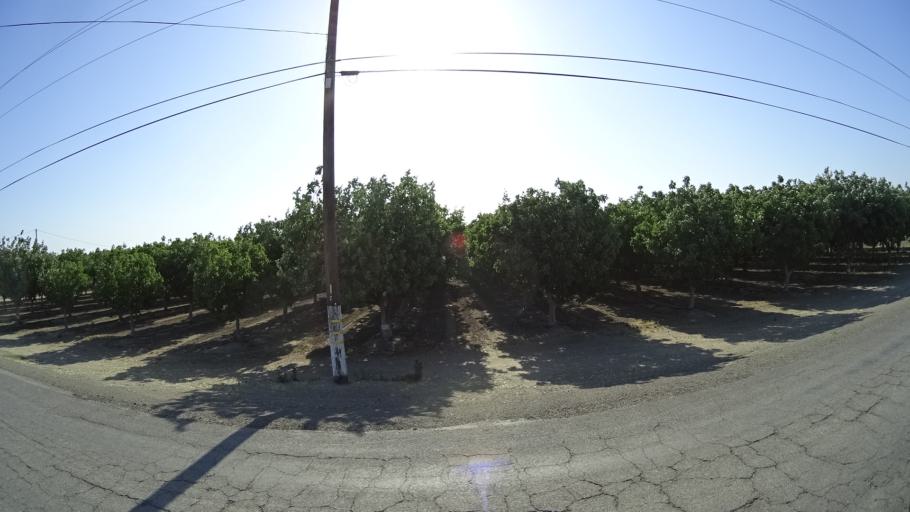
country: US
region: California
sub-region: Kings County
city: Home Garden
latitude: 36.3204
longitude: -119.5652
